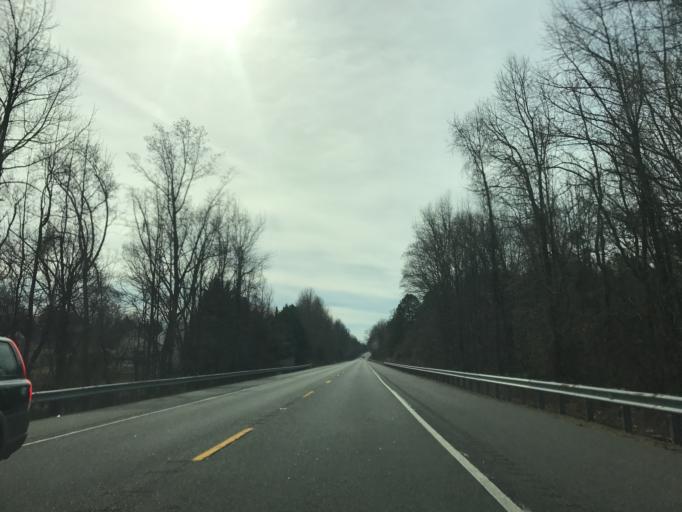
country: US
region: Maryland
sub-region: Queen Anne's County
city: Kingstown
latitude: 39.1457
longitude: -75.9848
